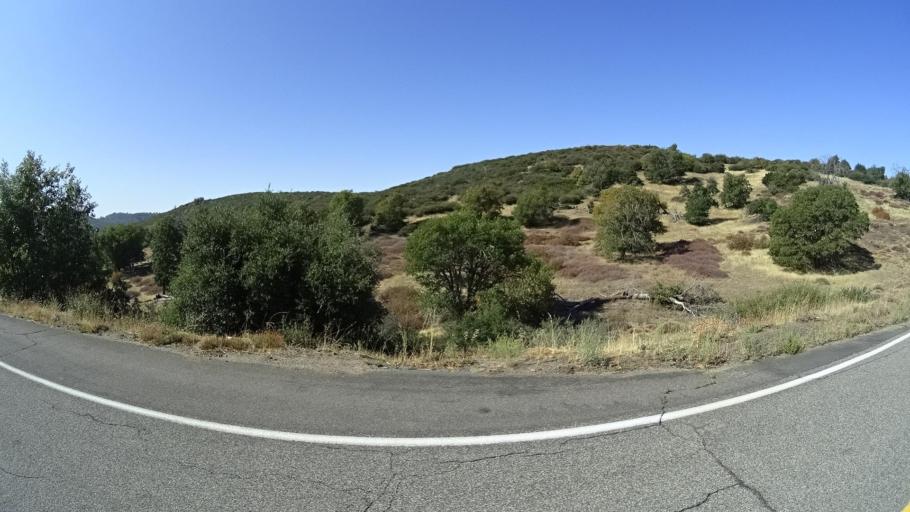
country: US
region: California
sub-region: San Diego County
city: Pine Valley
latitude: 32.9428
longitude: -116.4916
